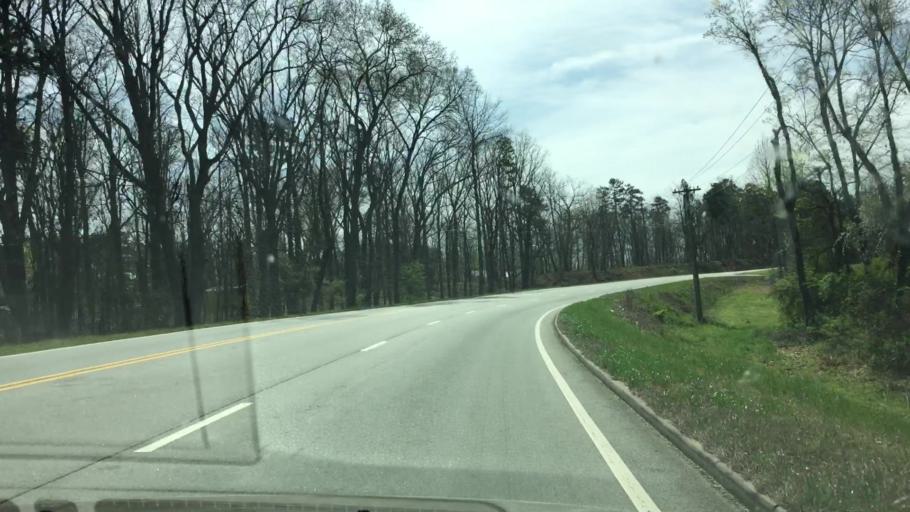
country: US
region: Georgia
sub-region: Barrow County
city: Winder
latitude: 34.0172
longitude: -83.7079
